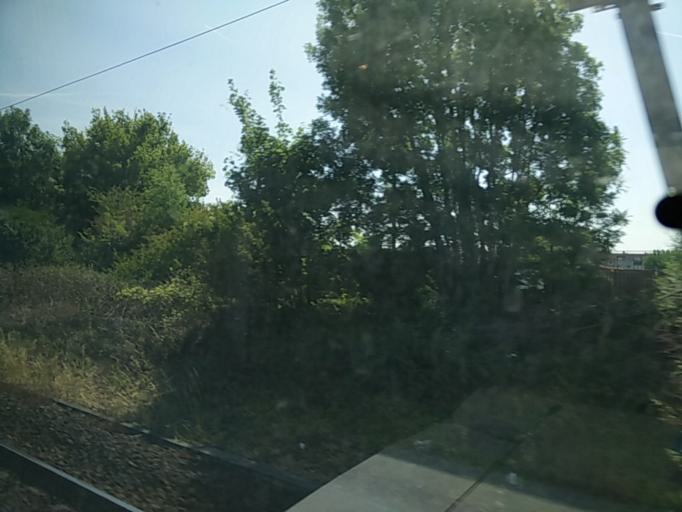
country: FR
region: Ile-de-France
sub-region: Departement du Val-de-Marne
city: Villiers-sur-Marne
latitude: 48.8256
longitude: 2.5498
